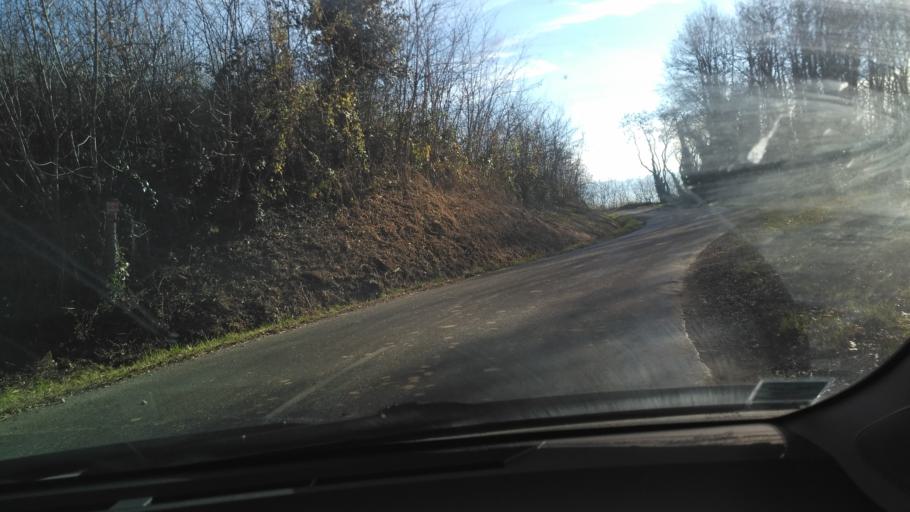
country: FR
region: Rhone-Alpes
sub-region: Departement de l'Isere
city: Saint-Antoine-l'Abbaye
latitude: 45.1587
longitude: 5.1823
